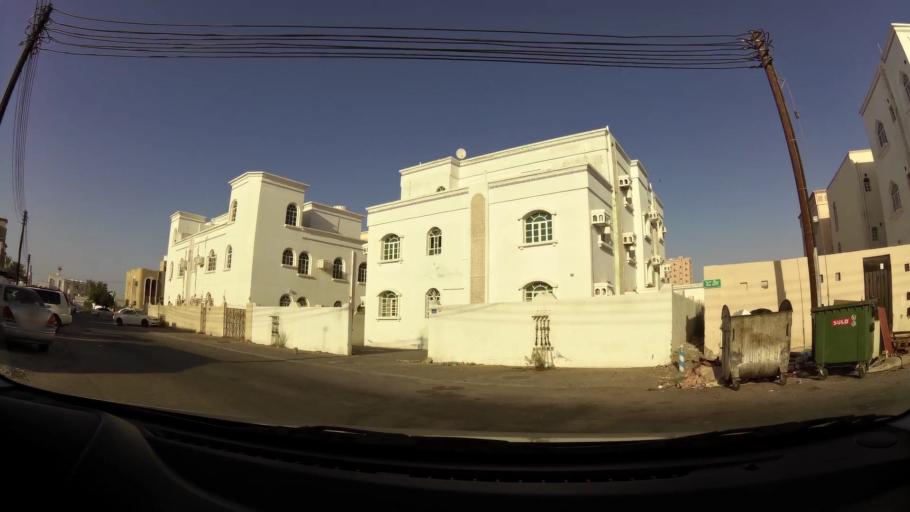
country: OM
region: Muhafazat Masqat
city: As Sib al Jadidah
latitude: 23.6299
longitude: 58.1938
